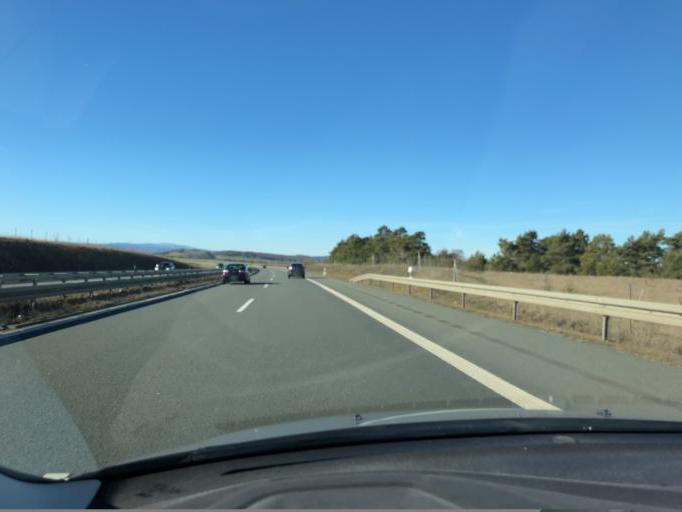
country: DE
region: Saxony-Anhalt
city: Quedlinburg
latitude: 51.8149
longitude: 11.1622
